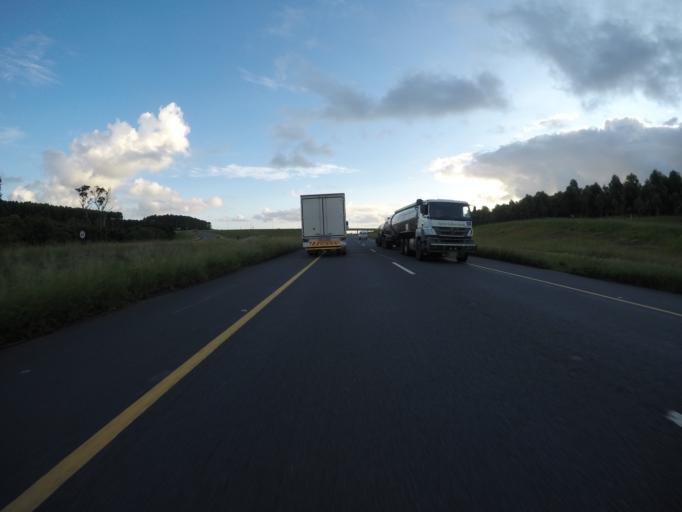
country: ZA
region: KwaZulu-Natal
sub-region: uThungulu District Municipality
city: KwaMbonambi
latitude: -28.5963
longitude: 32.0986
